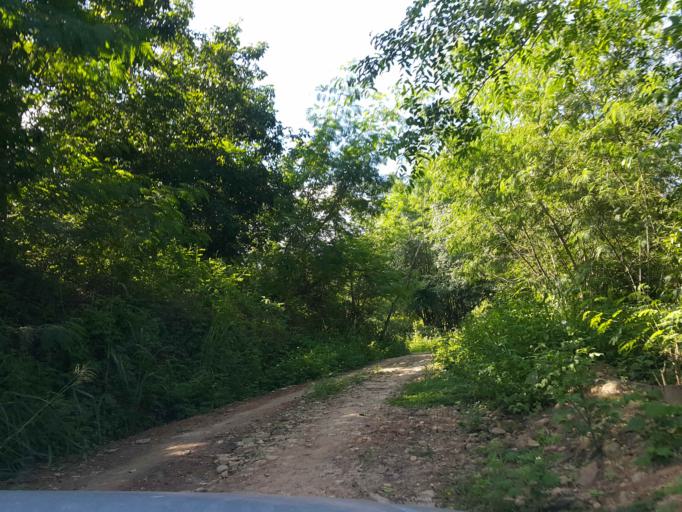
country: TH
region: Chiang Mai
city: Mae Taeng
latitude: 18.9744
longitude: 98.8854
